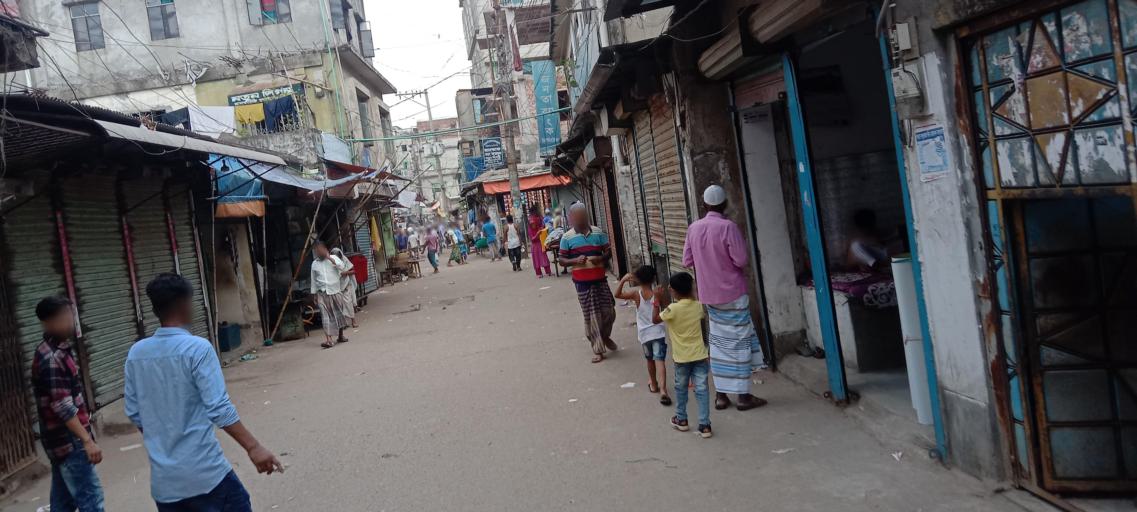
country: BD
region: Dhaka
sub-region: Dhaka
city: Dhaka
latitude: 23.7091
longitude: 90.3959
